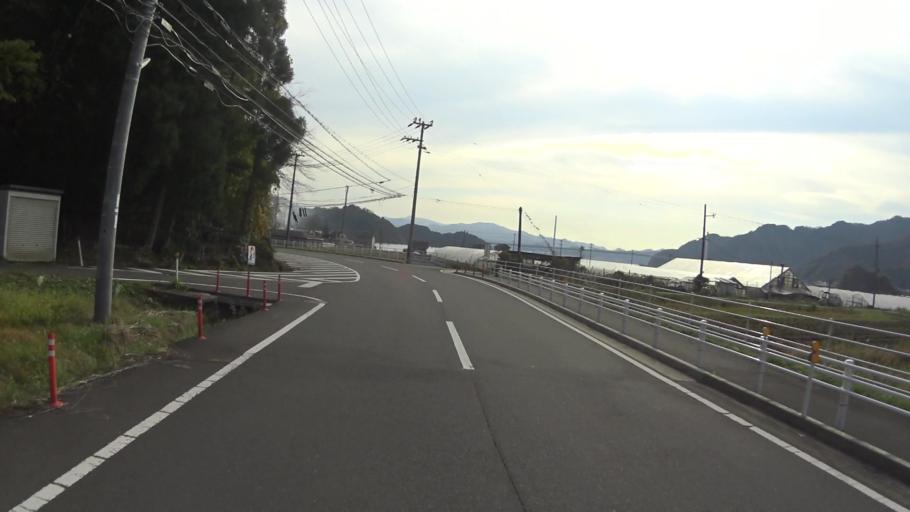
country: JP
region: Kyoto
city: Maizuru
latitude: 35.5207
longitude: 135.3907
